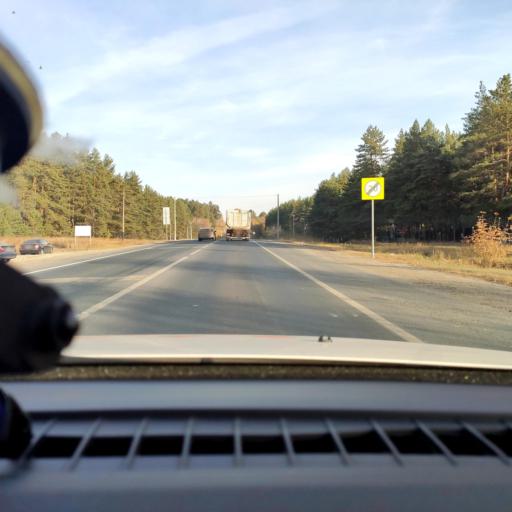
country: RU
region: Samara
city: Volzhskiy
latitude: 53.4391
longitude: 50.1242
